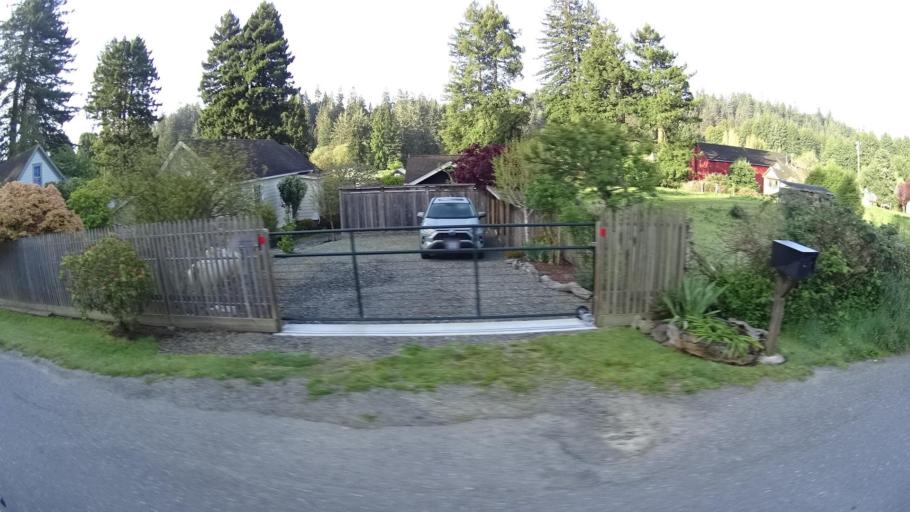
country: US
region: California
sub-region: Humboldt County
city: Myrtletown
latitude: 40.7610
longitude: -124.0598
